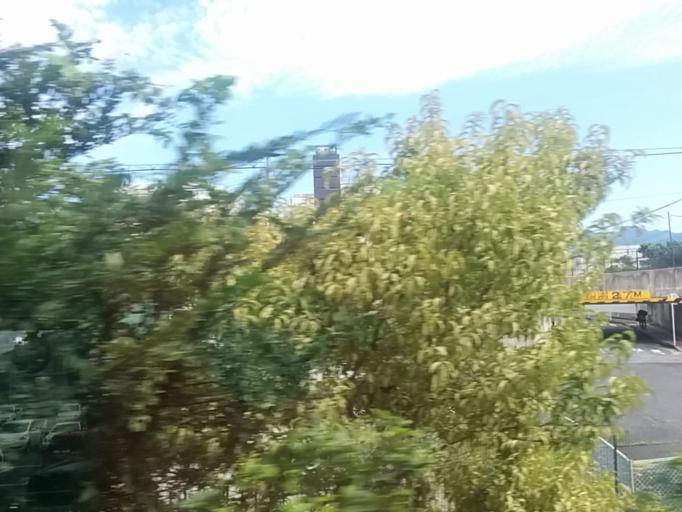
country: JP
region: Nara
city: Kashihara-shi
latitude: 34.5049
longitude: 135.7909
